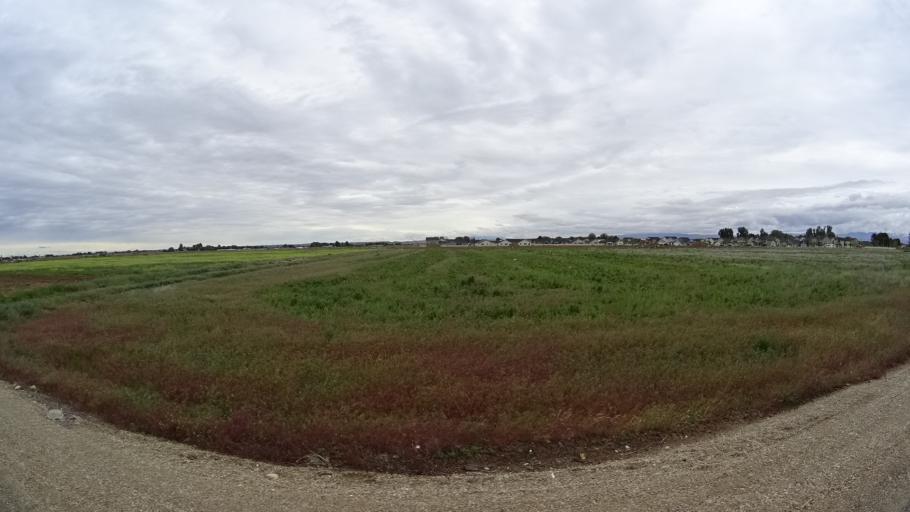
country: US
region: Idaho
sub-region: Ada County
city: Star
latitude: 43.6481
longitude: -116.4589
